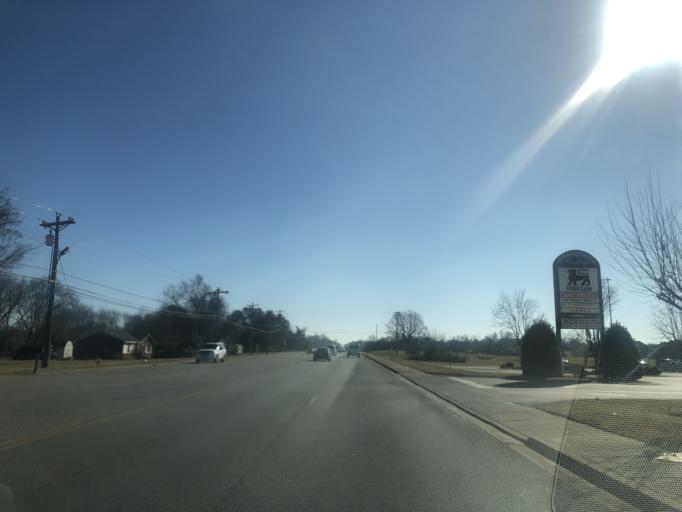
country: US
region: Tennessee
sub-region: Rutherford County
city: Smyrna
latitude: 35.9583
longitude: -86.5192
